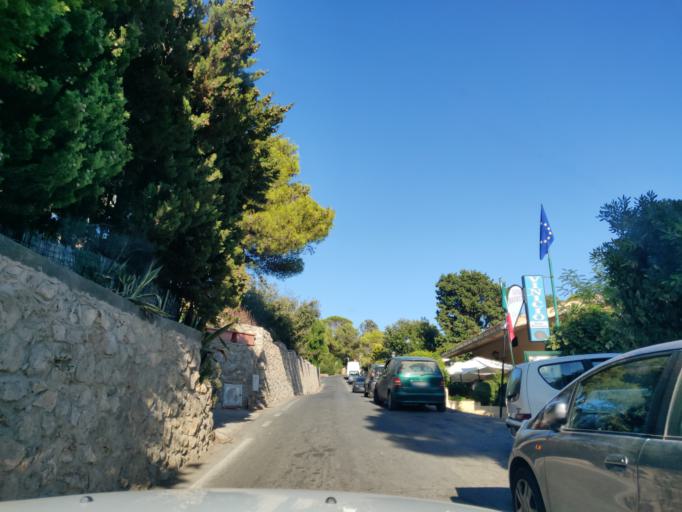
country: IT
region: Tuscany
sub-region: Provincia di Grosseto
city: Orbetello Scalo
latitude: 42.4073
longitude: 11.2875
